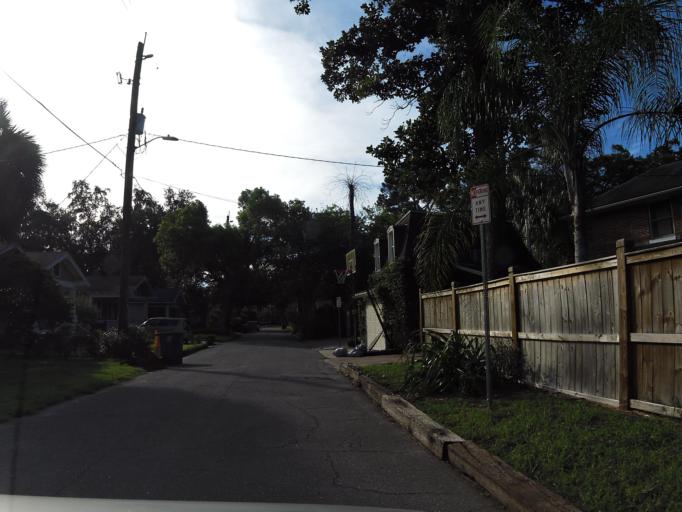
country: US
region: Florida
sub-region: Duval County
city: Jacksonville
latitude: 30.3019
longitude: -81.7035
